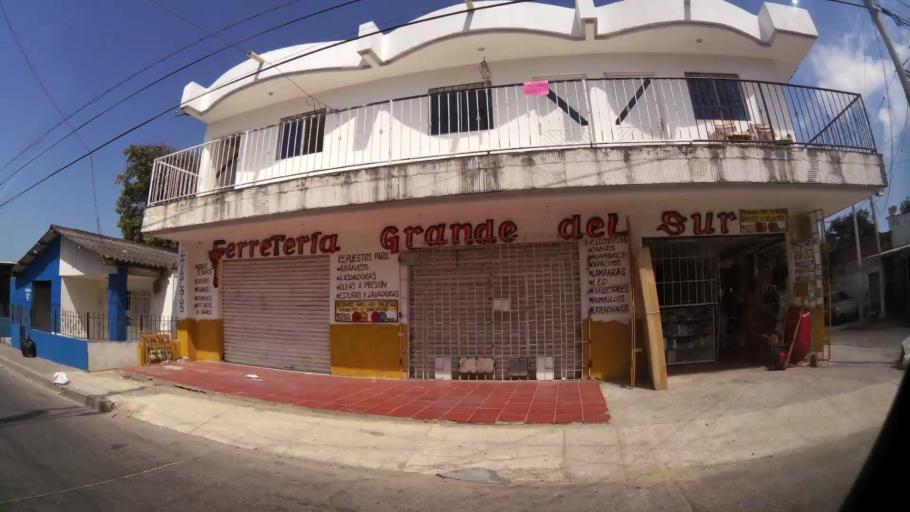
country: CO
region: Atlantico
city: Barranquilla
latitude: 10.9638
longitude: -74.8287
